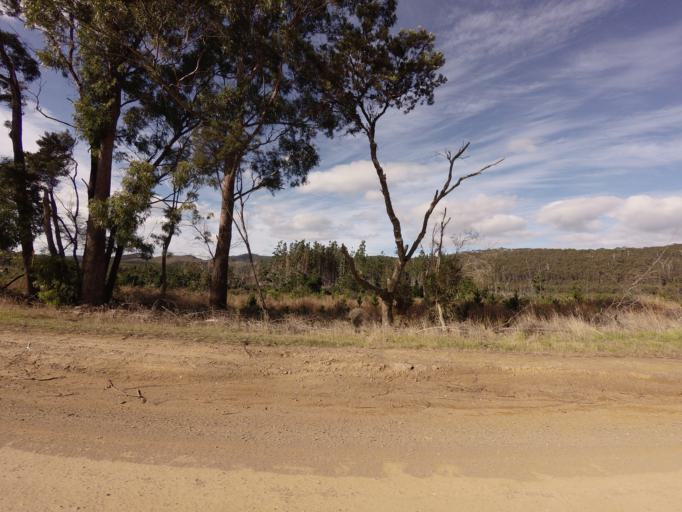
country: AU
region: Tasmania
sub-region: Clarence
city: Sandford
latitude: -43.1639
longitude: 147.7683
